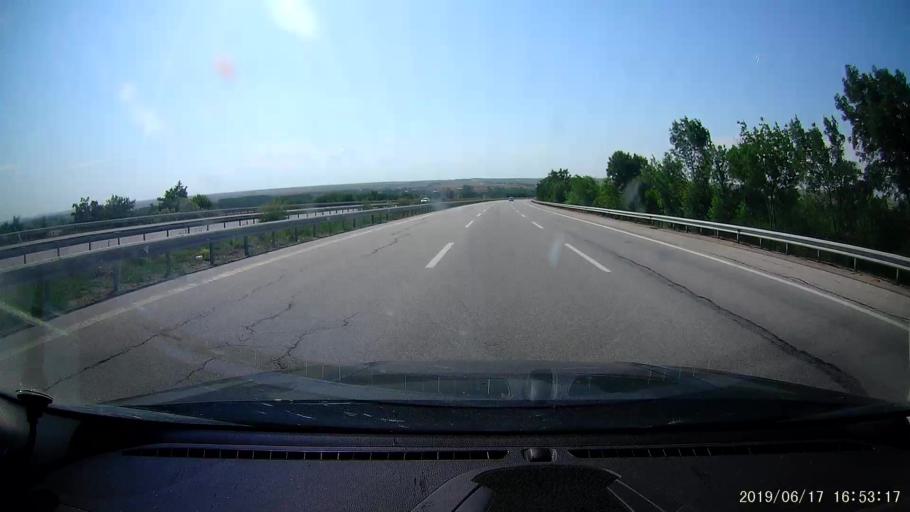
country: TR
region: Kirklareli
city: Inece
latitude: 41.5618
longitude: 27.0273
